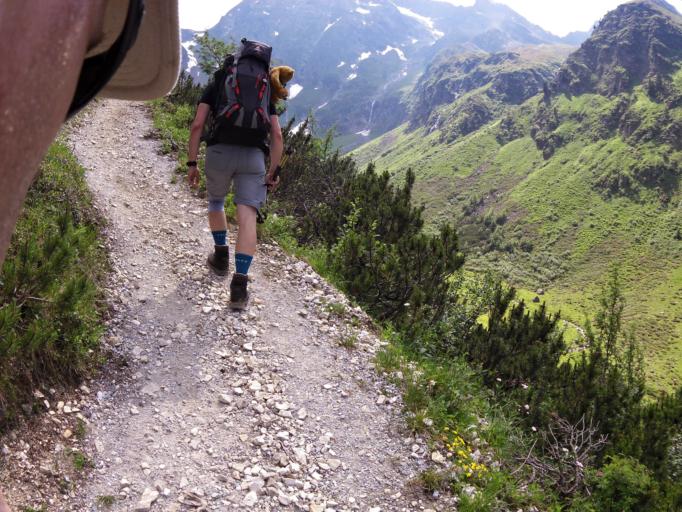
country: AT
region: Tyrol
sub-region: Politischer Bezirk Innsbruck Land
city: Gschnitz
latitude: 47.0601
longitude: 11.3167
